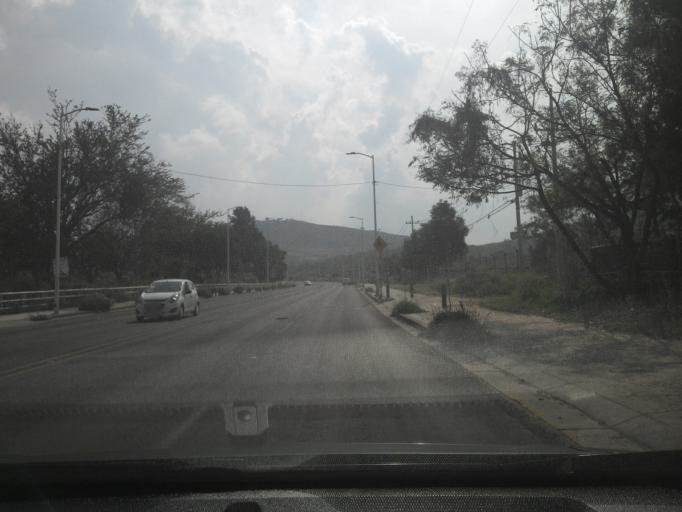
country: MX
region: Jalisco
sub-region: Tlajomulco de Zuniga
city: Lomas del Sur
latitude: 20.4967
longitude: -103.4176
